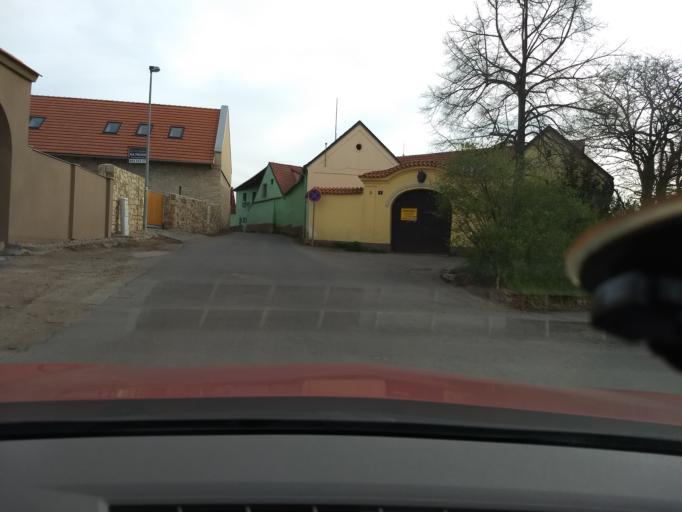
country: CZ
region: Central Bohemia
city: Roztoky
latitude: 50.1405
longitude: 14.3724
